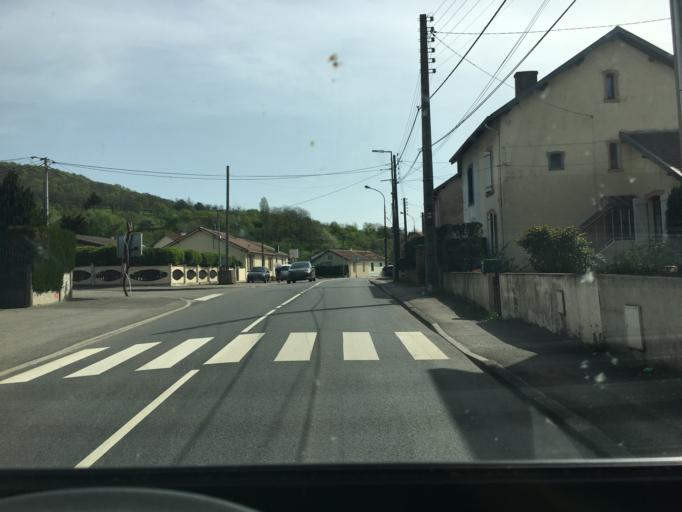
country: FR
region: Lorraine
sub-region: Departement de Meurthe-et-Moselle
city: Neuves-Maisons
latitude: 48.6133
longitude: 6.1202
